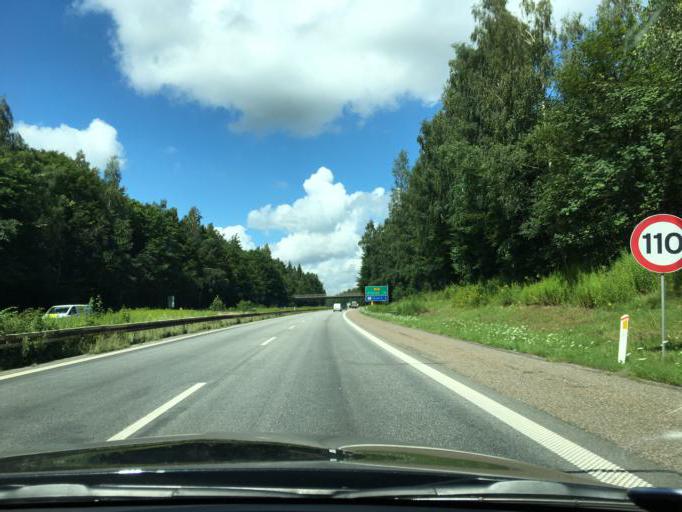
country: DK
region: Capital Region
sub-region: Fureso Kommune
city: Vaerlose
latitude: 55.7839
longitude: 12.3926
